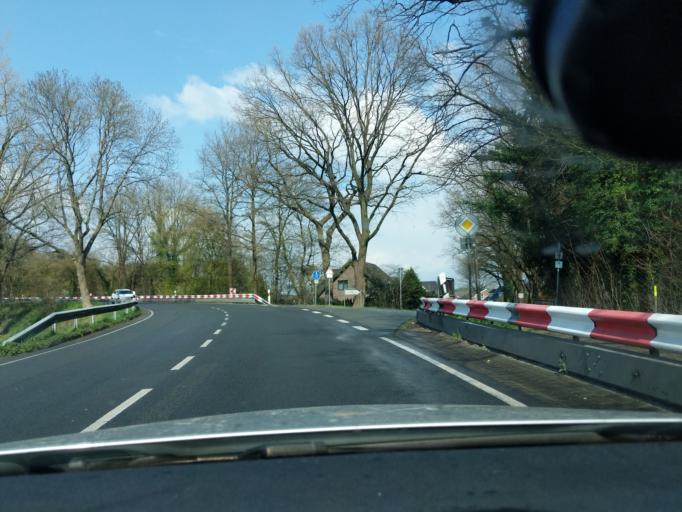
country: DE
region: Lower Saxony
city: Harsefeld
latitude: 53.4619
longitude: 9.5035
